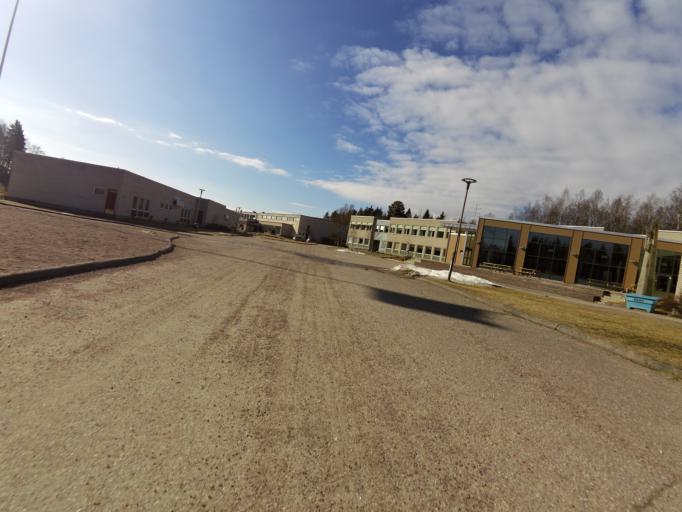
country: SE
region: Gaevleborg
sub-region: Hofors Kommun
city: Hofors
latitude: 60.5475
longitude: 16.2701
